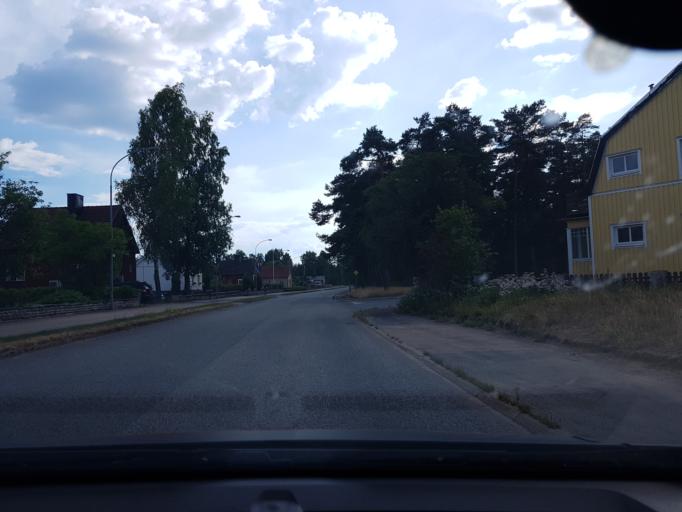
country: SE
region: Joenkoeping
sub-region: Gislaveds Kommun
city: Gislaved
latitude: 57.2906
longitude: 13.5560
